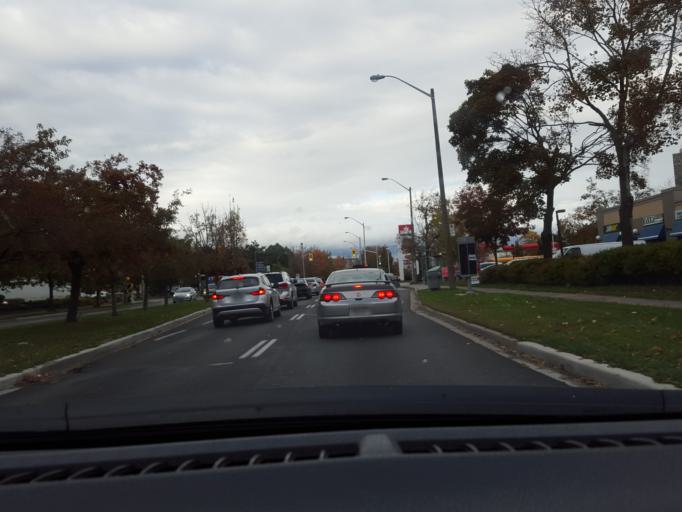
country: CA
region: Ontario
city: Toronto
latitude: 43.7043
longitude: -79.3505
